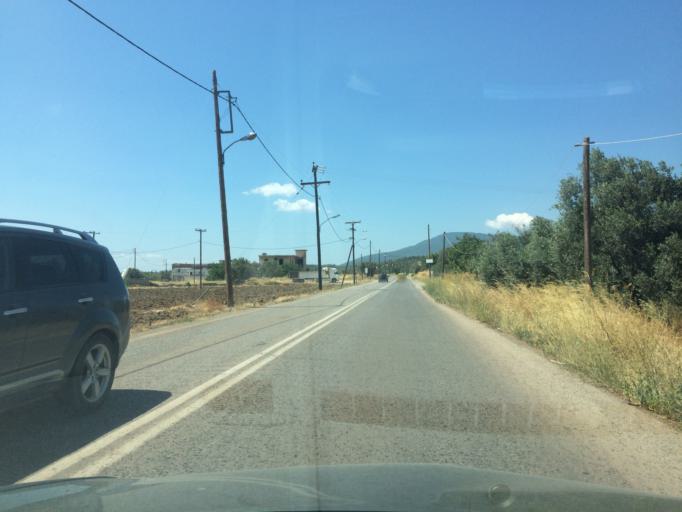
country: GR
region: Central Greece
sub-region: Nomos Evvoias
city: Psachna
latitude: 38.5779
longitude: 23.6291
